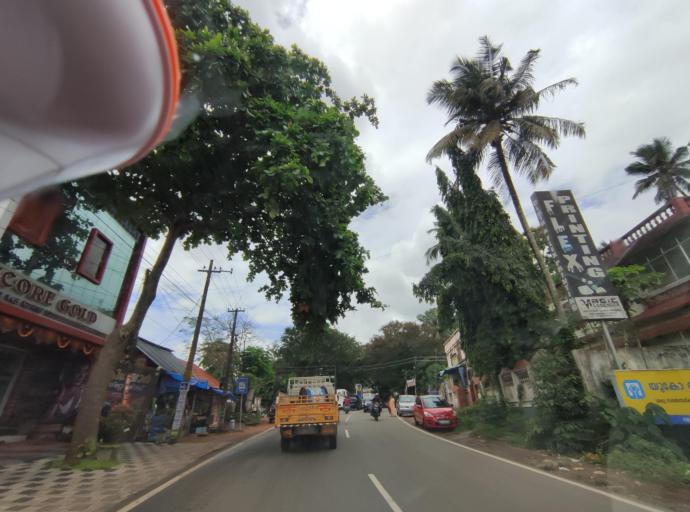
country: IN
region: Kerala
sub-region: Thiruvananthapuram
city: Nedumangad
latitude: 8.5889
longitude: 76.9501
